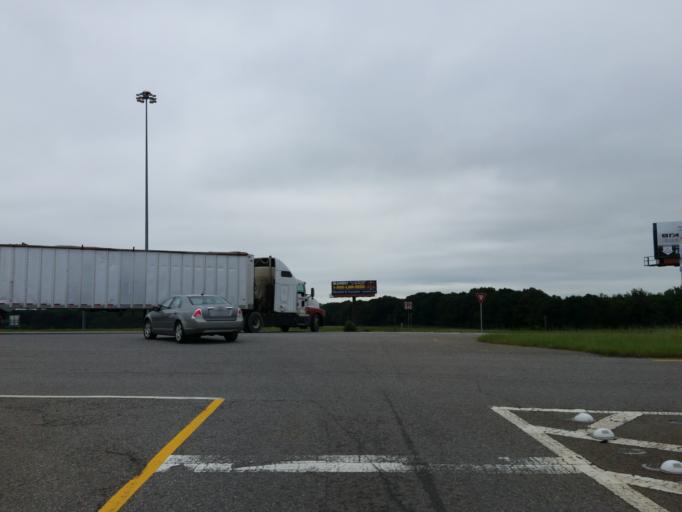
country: US
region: Georgia
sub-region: Houston County
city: Perry
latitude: 32.4323
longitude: -83.7584
